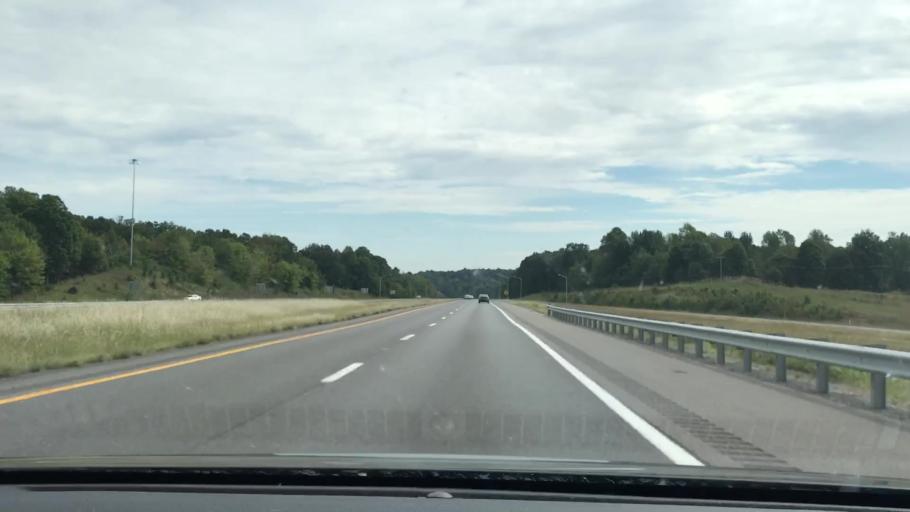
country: US
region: Kentucky
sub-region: Lyon County
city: Eddyville
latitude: 37.0737
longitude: -88.1211
